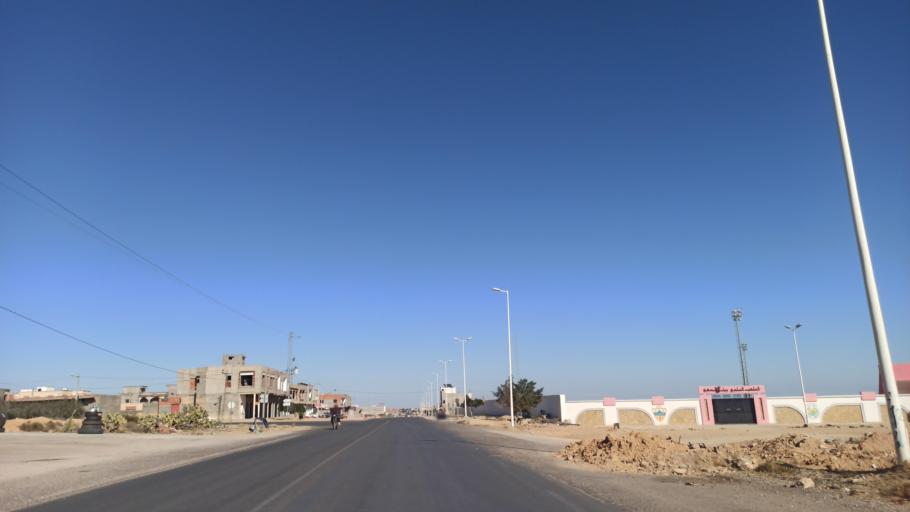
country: TN
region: Sidi Bu Zayd
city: Bi'r al Hufayy
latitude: 34.9419
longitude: 9.2042
